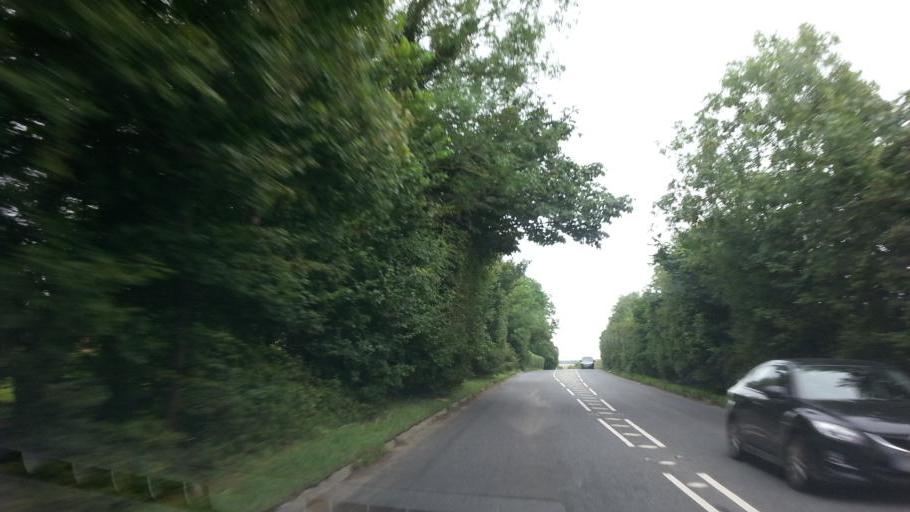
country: GB
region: England
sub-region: Wiltshire
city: Westbury
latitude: 51.2832
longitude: -2.1844
